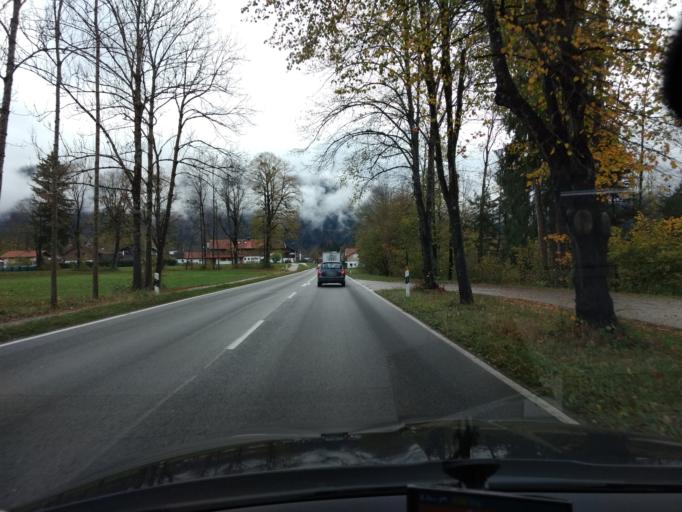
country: DE
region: Bavaria
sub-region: Upper Bavaria
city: Lenggries
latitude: 47.6397
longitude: 11.5935
